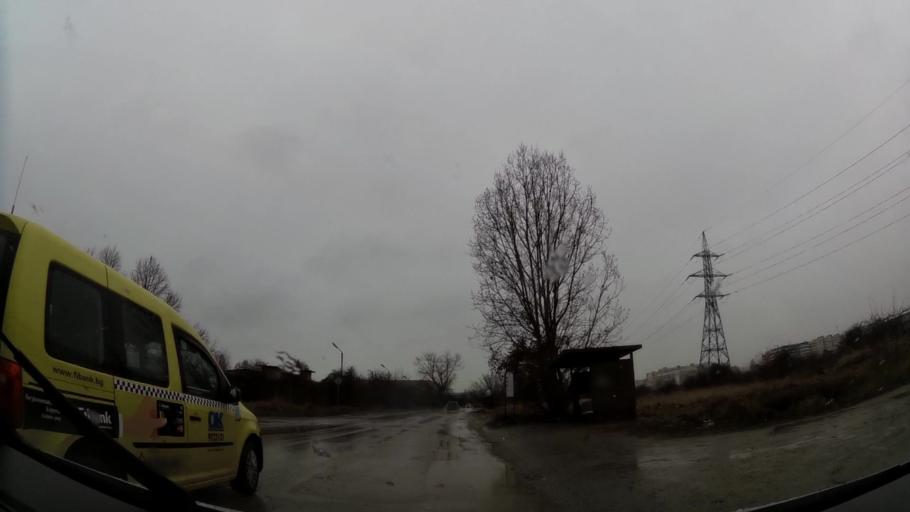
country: BG
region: Sofia-Capital
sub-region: Stolichna Obshtina
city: Sofia
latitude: 42.6494
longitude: 23.4136
